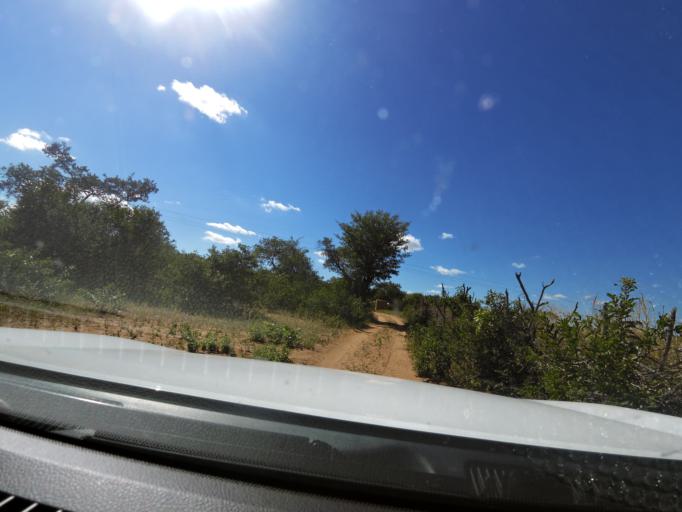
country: ZW
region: Matabeleland North
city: Kamativi Mine
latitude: -17.9698
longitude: 27.1416
